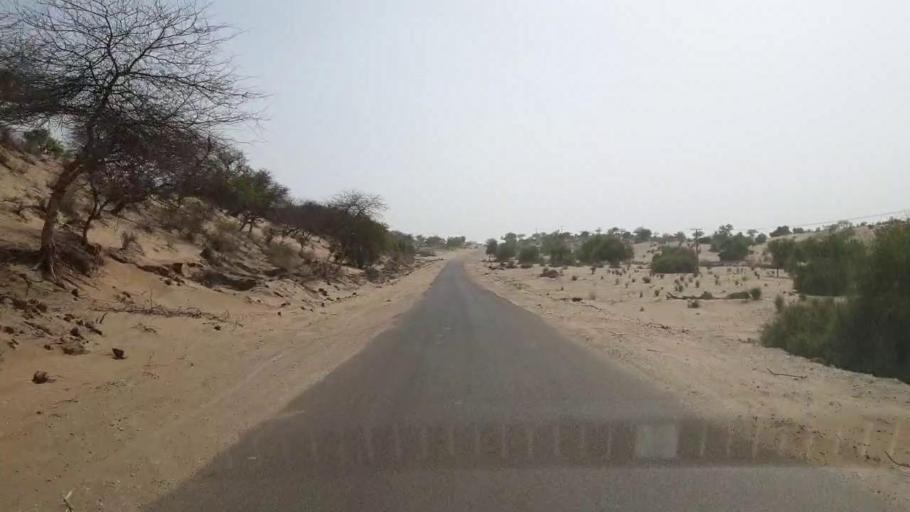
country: PK
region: Sindh
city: Mithi
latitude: 24.6222
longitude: 69.9023
